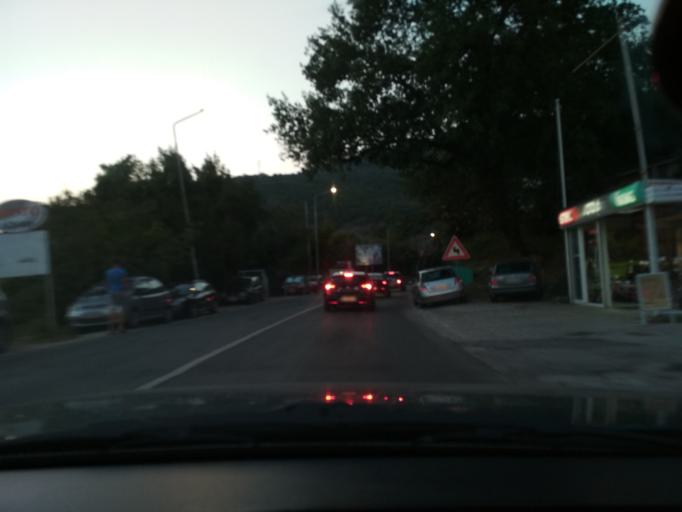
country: ME
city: Igalo
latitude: 42.4592
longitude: 18.5214
